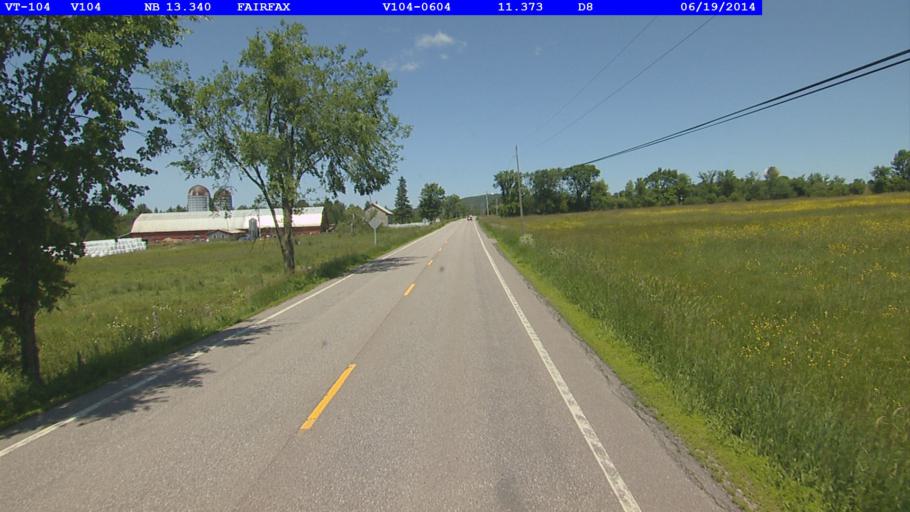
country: US
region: Vermont
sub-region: Franklin County
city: Saint Albans
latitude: 44.7477
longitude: -73.0526
